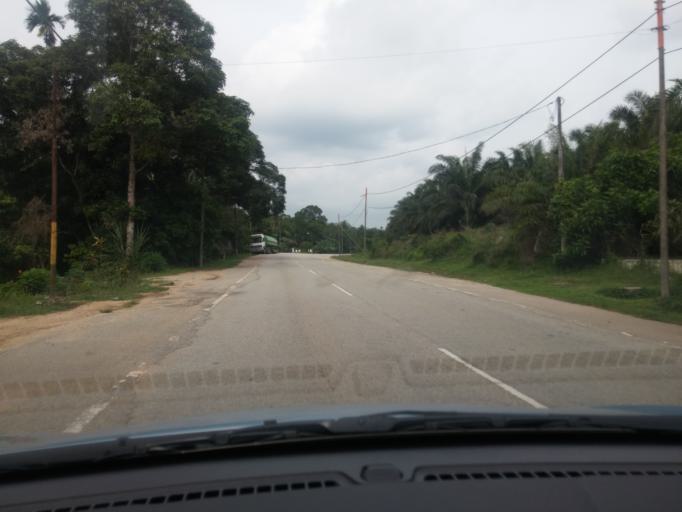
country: MY
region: Pahang
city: Kuantan
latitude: 3.8837
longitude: 103.1637
